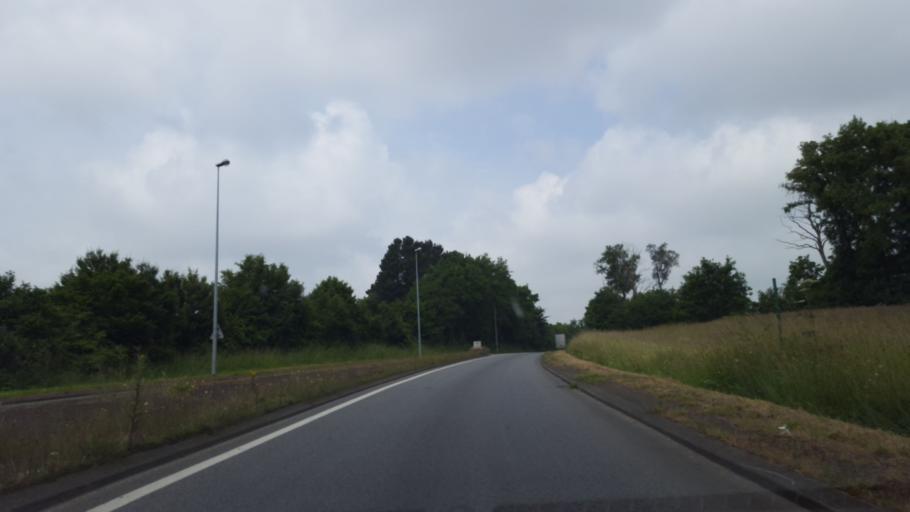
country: FR
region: Brittany
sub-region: Departement d'Ille-et-Vilaine
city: Chartres-de-Bretagne
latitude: 48.0430
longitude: -1.6961
